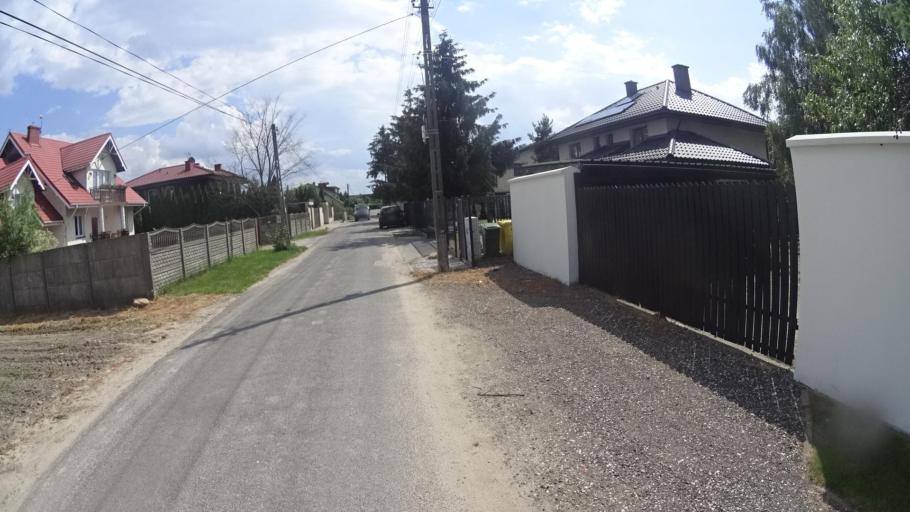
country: PL
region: Masovian Voivodeship
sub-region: Powiat pruszkowski
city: Piastow
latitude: 52.2016
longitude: 20.8504
